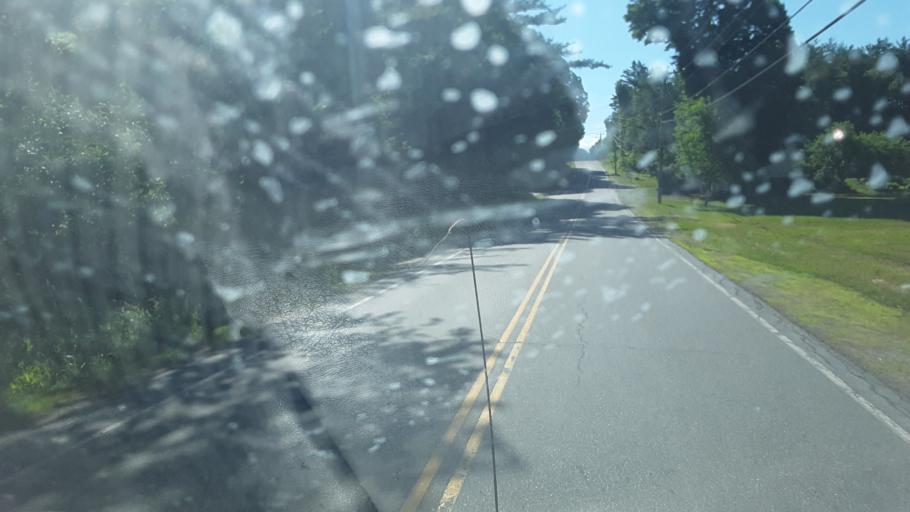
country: US
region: New Hampshire
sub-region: Grafton County
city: North Haverhill
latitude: 44.0818
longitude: -72.0013
